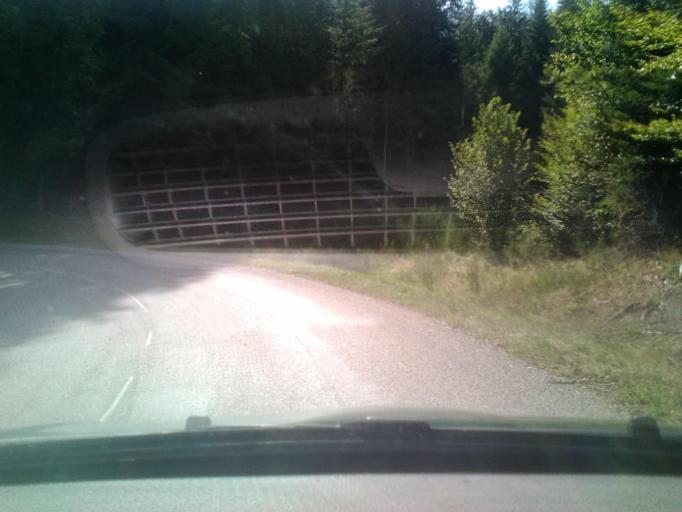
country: FR
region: Lorraine
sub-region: Departement des Vosges
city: Bruyeres
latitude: 48.2721
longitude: 6.7886
